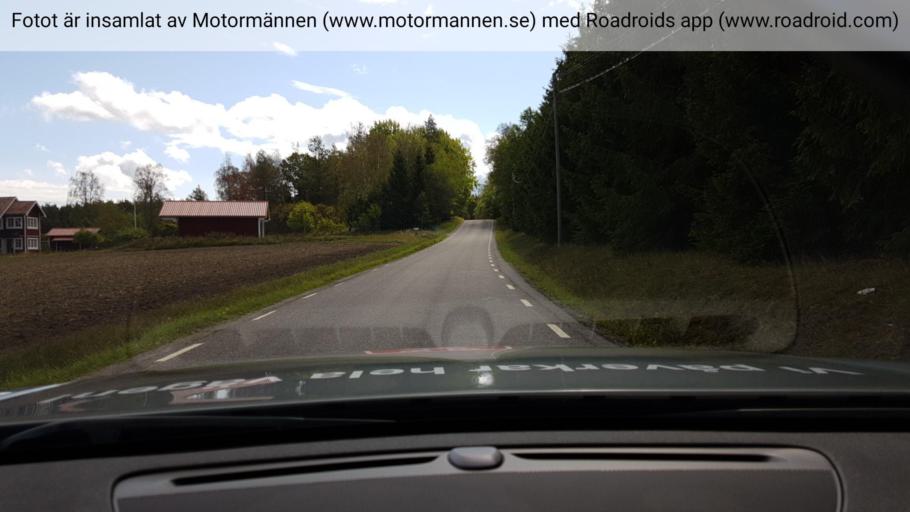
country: SE
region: Soedermanland
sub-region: Strangnas Kommun
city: Stallarholmen
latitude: 59.3971
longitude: 17.2652
